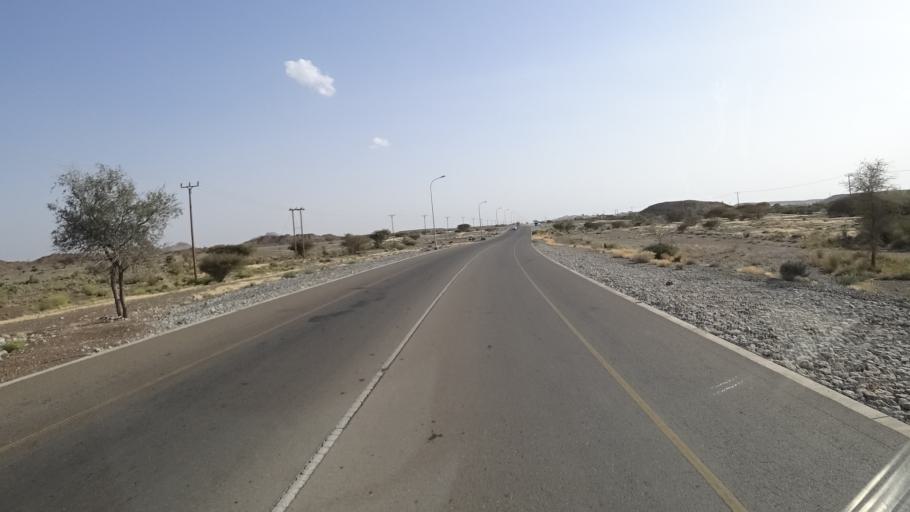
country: OM
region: Muhafazat ad Dakhiliyah
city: Izki
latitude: 22.8687
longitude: 57.7605
